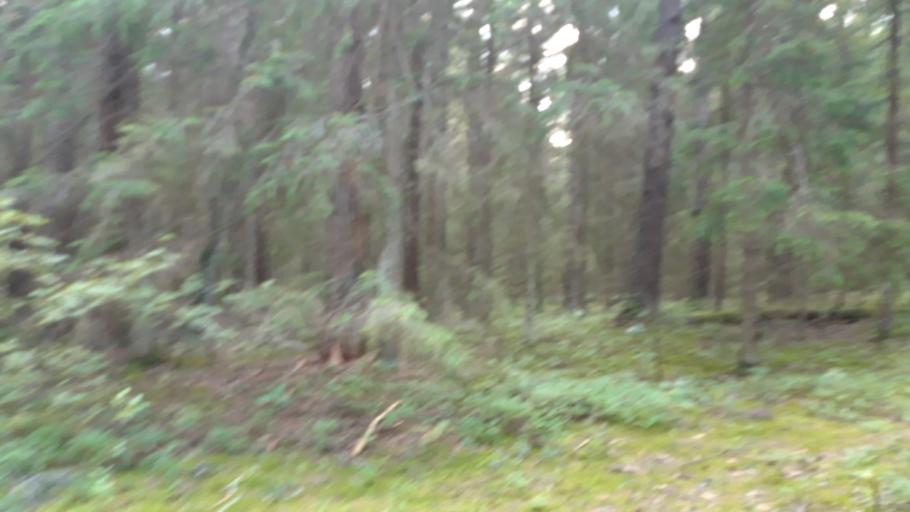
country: RU
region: Tverskaya
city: Konakovo
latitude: 56.6945
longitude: 36.7228
